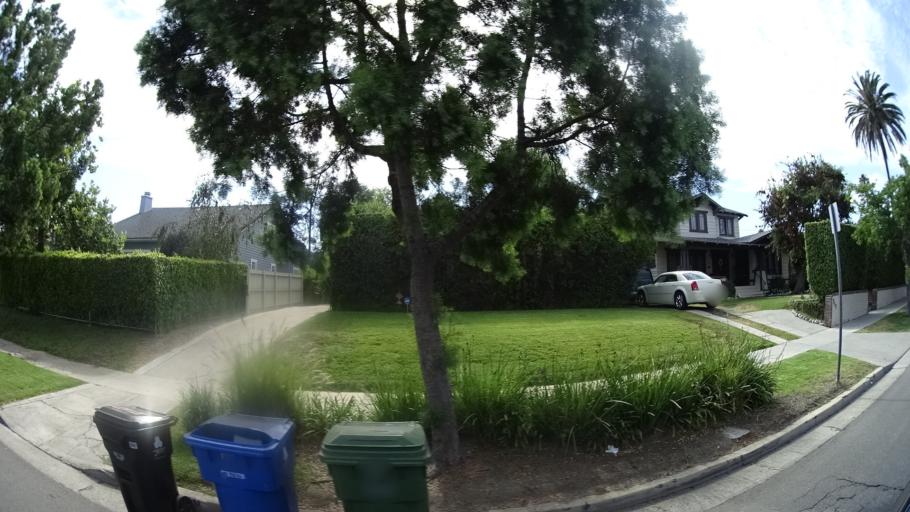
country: US
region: California
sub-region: Los Angeles County
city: Hollywood
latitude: 34.0752
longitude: -118.3136
